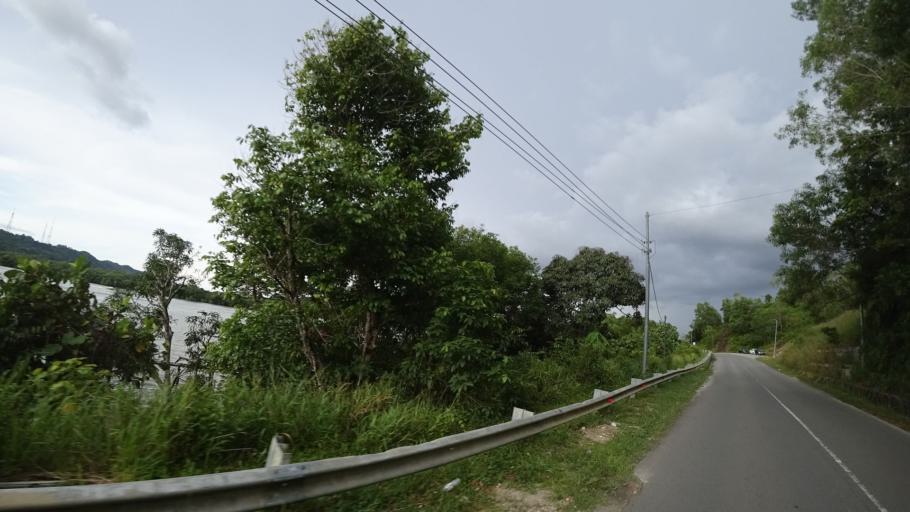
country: BN
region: Brunei and Muara
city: Bandar Seri Begawan
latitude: 4.8609
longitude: 114.9501
